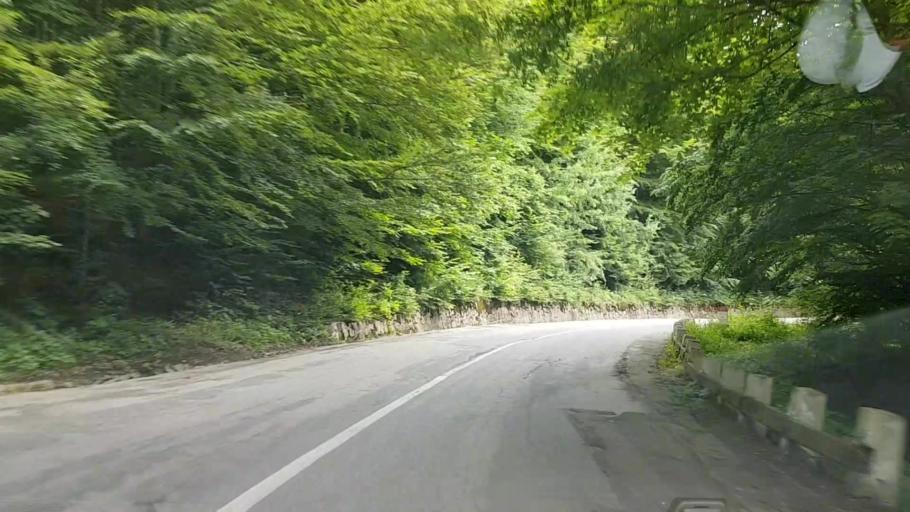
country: RO
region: Neamt
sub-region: Comuna Pangarati
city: Pangarati
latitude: 46.9871
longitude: 26.1178
